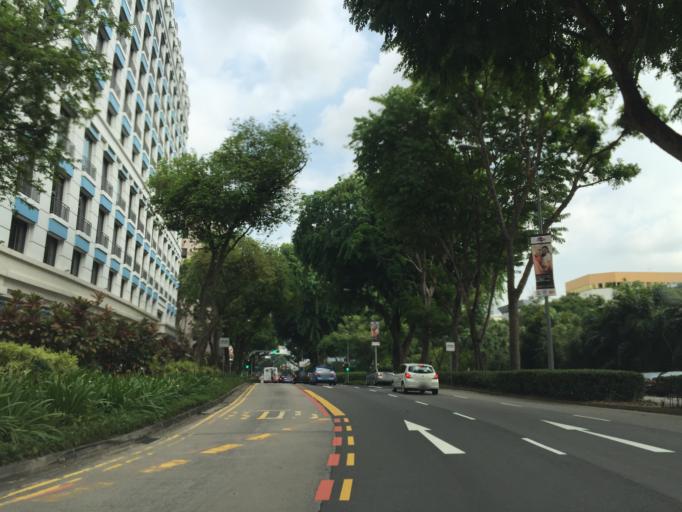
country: SG
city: Singapore
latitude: 1.2996
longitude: 103.8425
